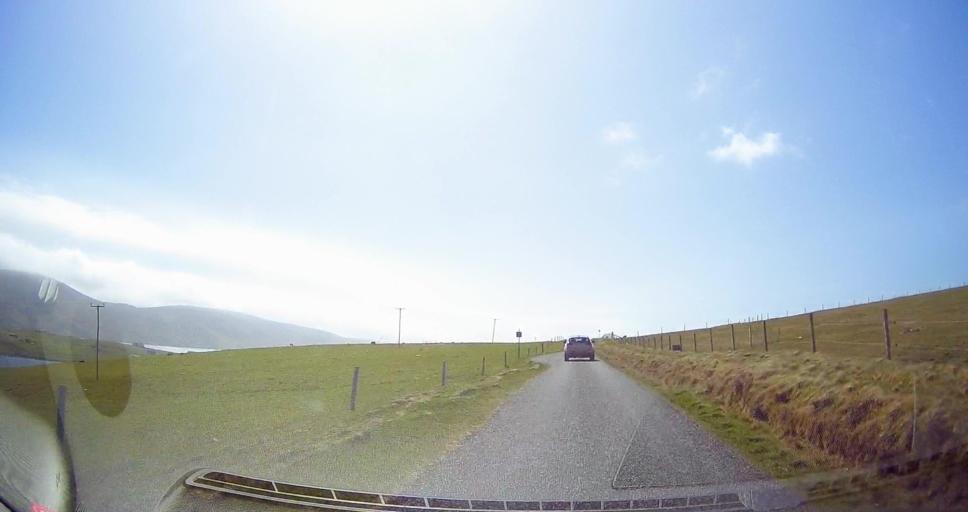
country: GB
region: Scotland
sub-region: Shetland Islands
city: Sandwick
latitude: 60.0768
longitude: -1.3383
